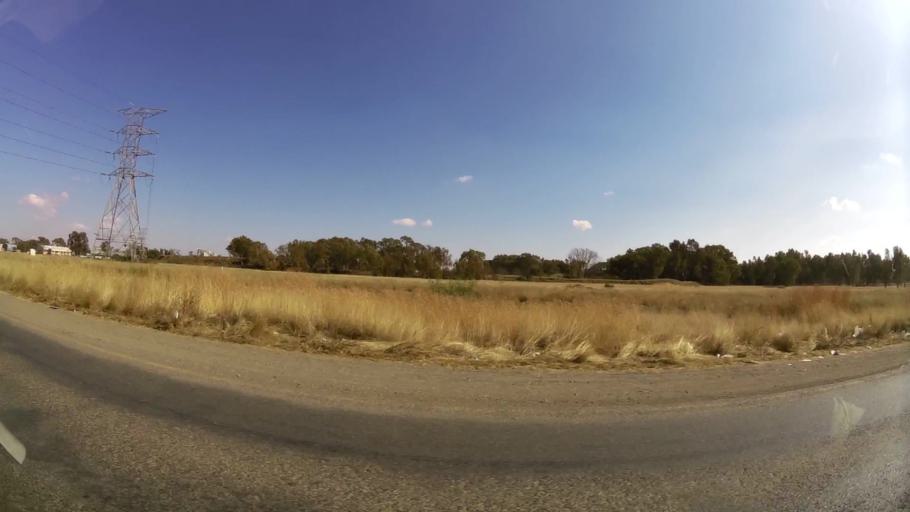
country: ZA
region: Orange Free State
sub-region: Mangaung Metropolitan Municipality
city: Bloemfontein
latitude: -29.1247
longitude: 26.2671
